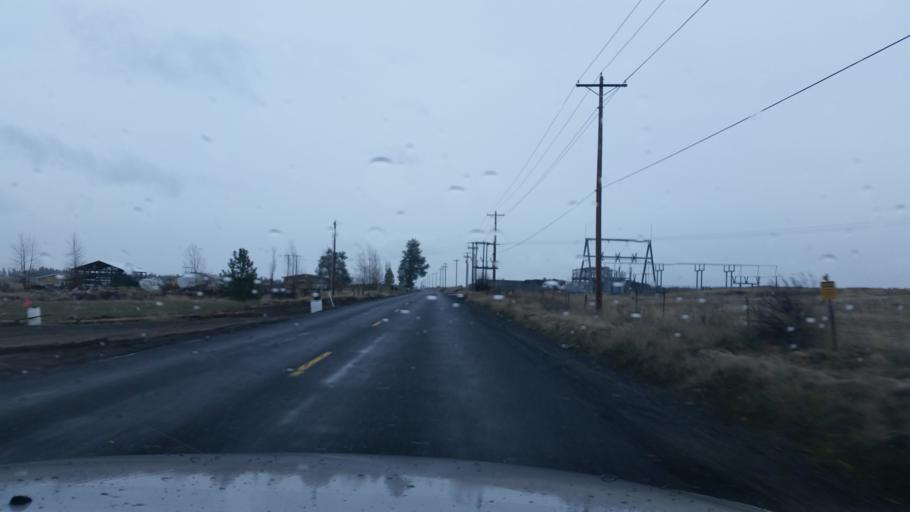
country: US
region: Washington
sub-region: Spokane County
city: Airway Heights
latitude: 47.6718
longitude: -117.5757
